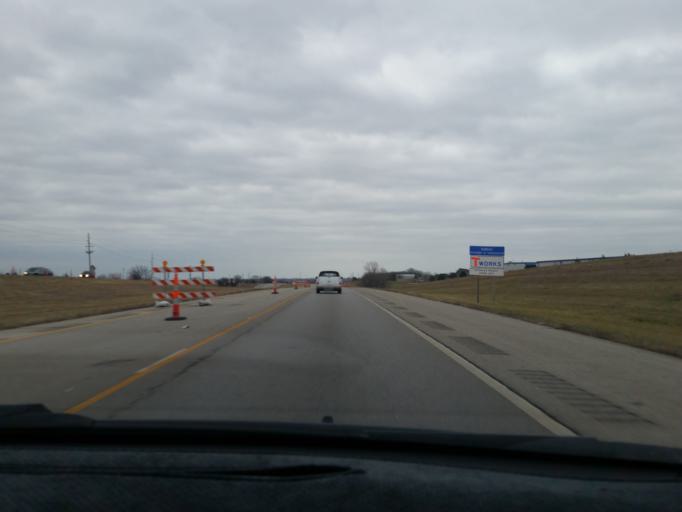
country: US
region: Kansas
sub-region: Douglas County
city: Lawrence
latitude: 38.9423
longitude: -95.1947
